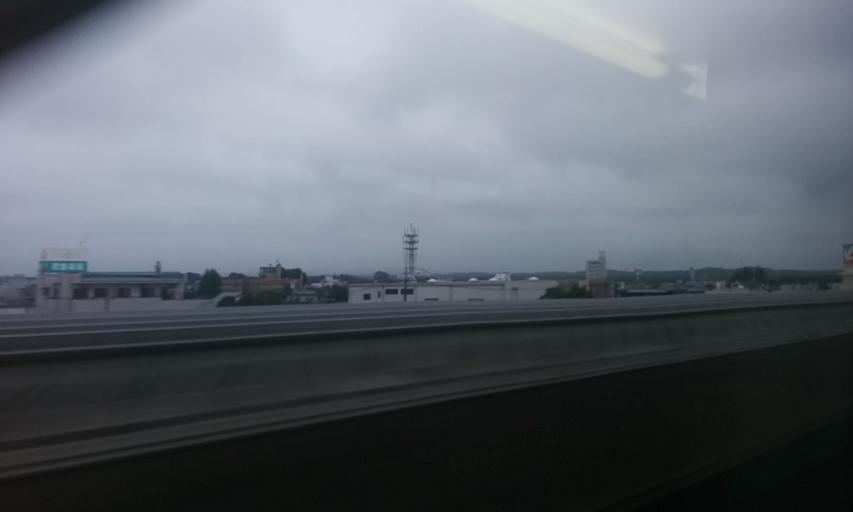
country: JP
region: Tochigi
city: Kuroiso
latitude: 36.9662
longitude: 140.0563
